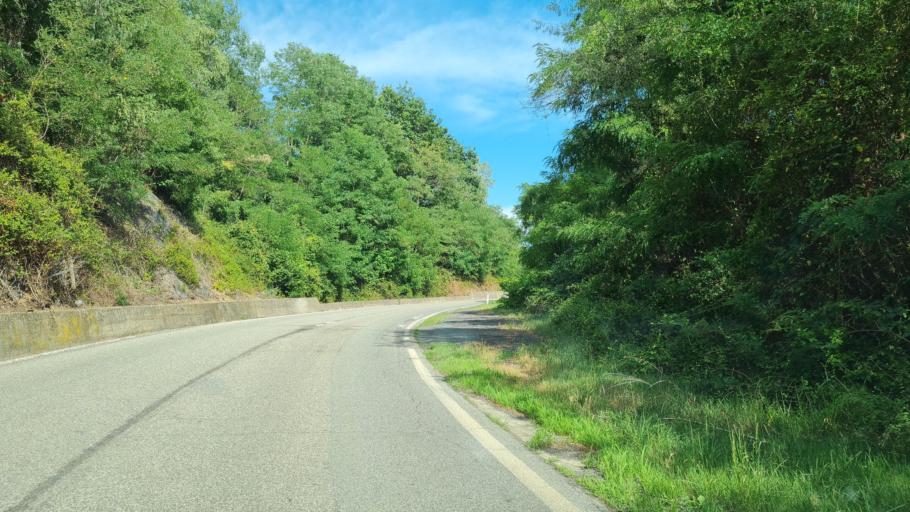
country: IT
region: Piedmont
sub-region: Provincia di Biella
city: Lessona
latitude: 45.5917
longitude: 8.2055
